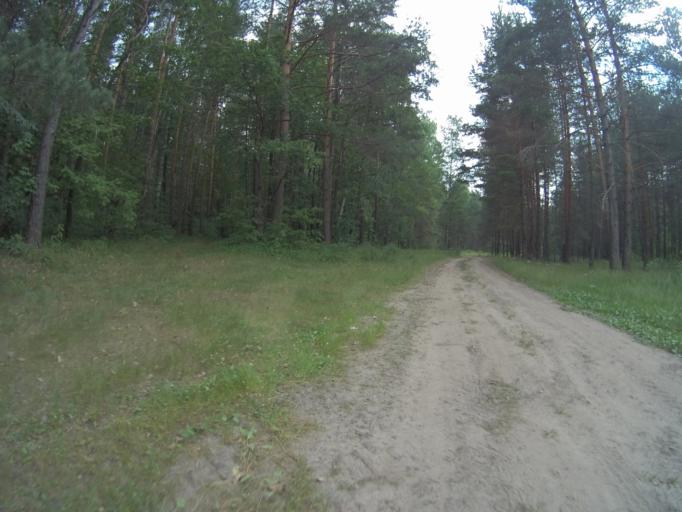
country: RU
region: Vladimir
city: Kommunar
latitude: 56.1105
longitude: 40.4906
